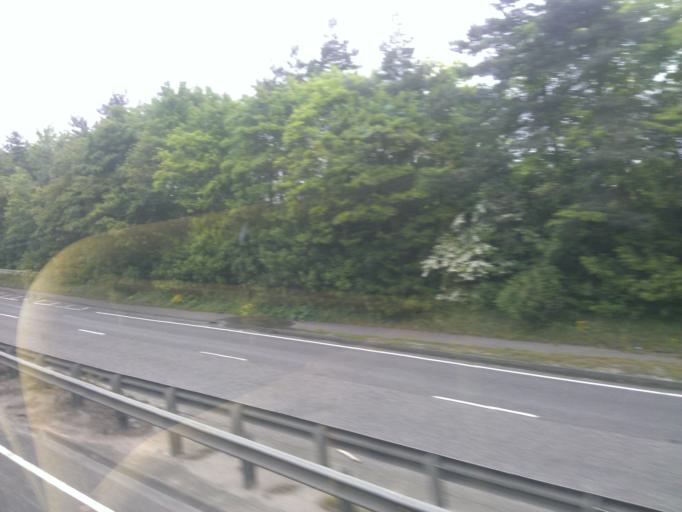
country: GB
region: England
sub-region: Suffolk
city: East Bergholt
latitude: 51.9450
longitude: 0.9570
